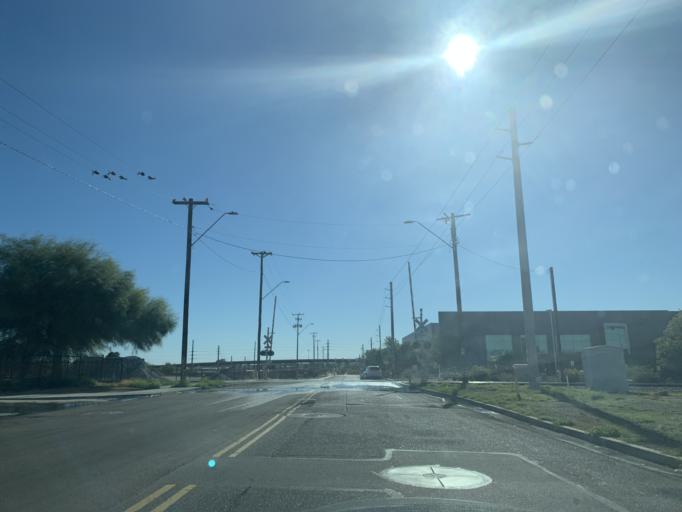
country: US
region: Arizona
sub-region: Maricopa County
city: Tempe Junction
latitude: 33.4441
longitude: -111.9785
